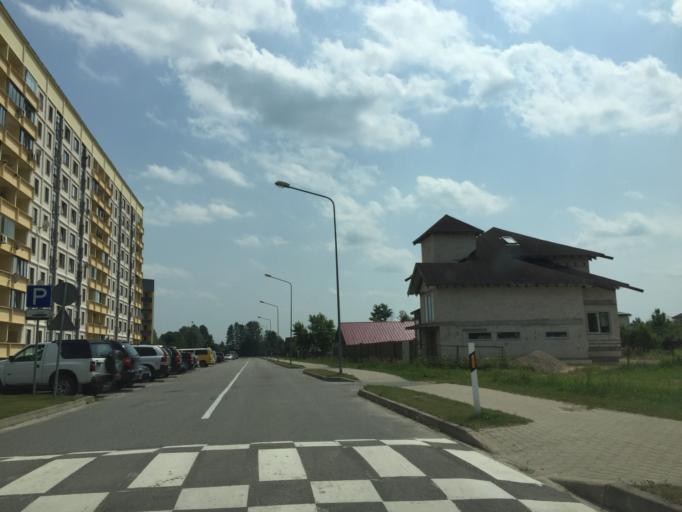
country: LV
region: Olaine
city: Olaine
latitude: 56.7790
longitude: 23.9231
